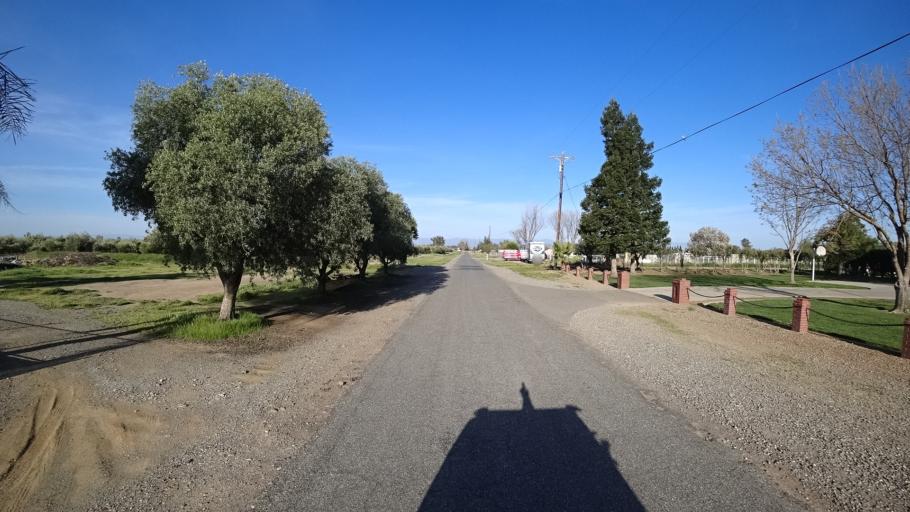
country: US
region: California
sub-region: Glenn County
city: Orland
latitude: 39.7332
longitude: -122.2188
